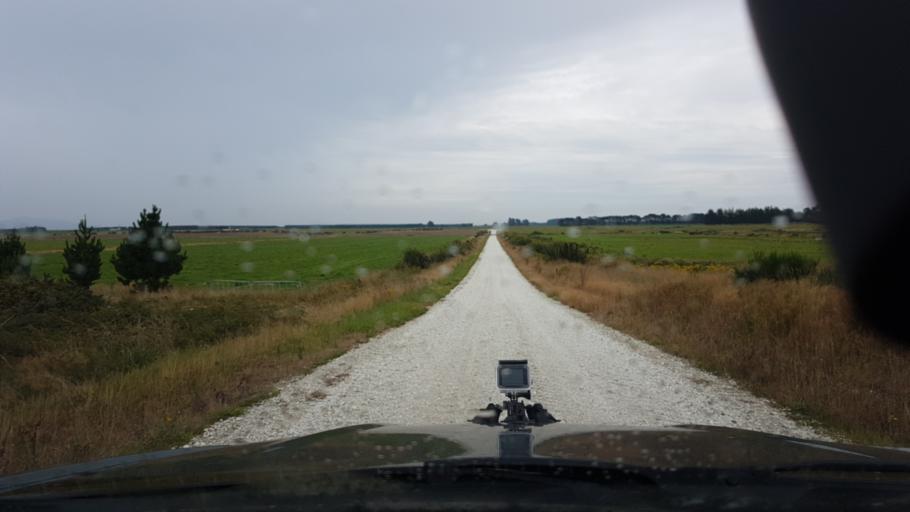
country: NZ
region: Southland
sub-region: Invercargill City
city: Invercargill
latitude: -46.5011
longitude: 168.4081
